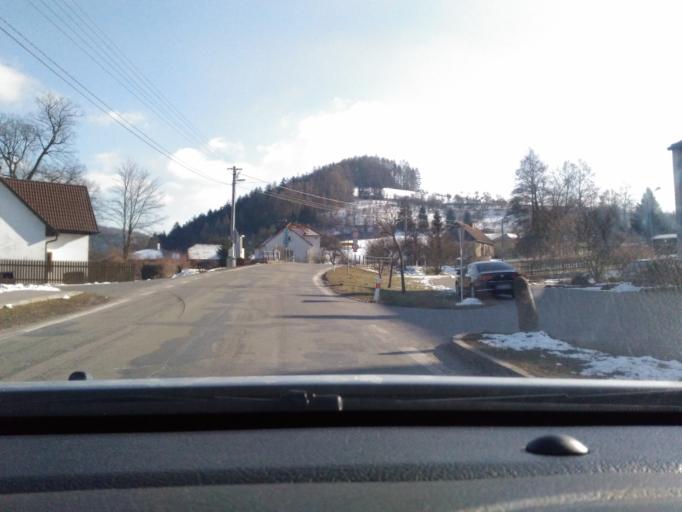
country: CZ
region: South Moravian
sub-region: Okres Brno-Venkov
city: Nedvedice
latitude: 49.4828
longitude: 16.3348
